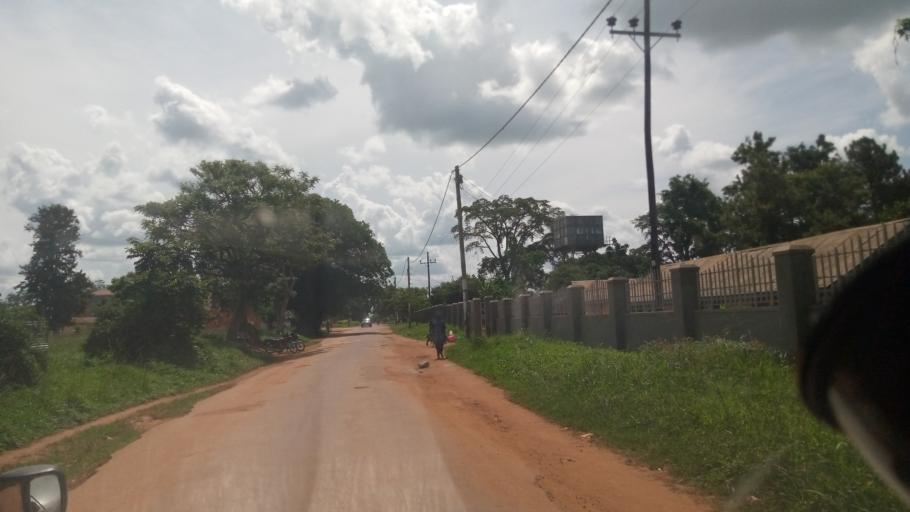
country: UG
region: Northern Region
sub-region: Lira District
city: Lira
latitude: 2.2508
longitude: 32.9015
